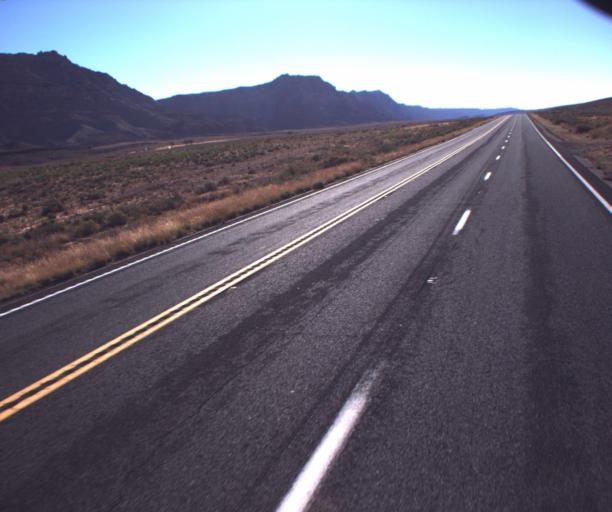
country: US
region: Arizona
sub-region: Coconino County
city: LeChee
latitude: 36.5903
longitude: -111.6538
